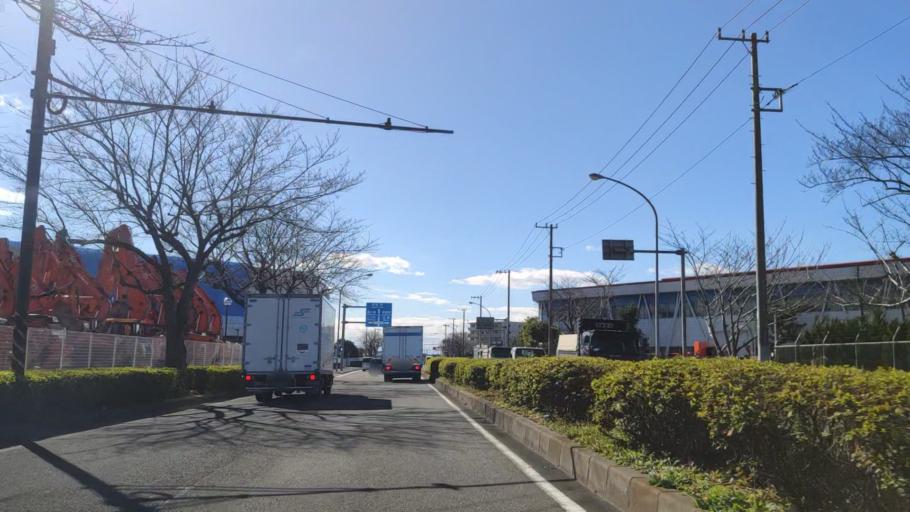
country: JP
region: Kanagawa
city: Minami-rinkan
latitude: 35.5000
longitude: 139.4839
